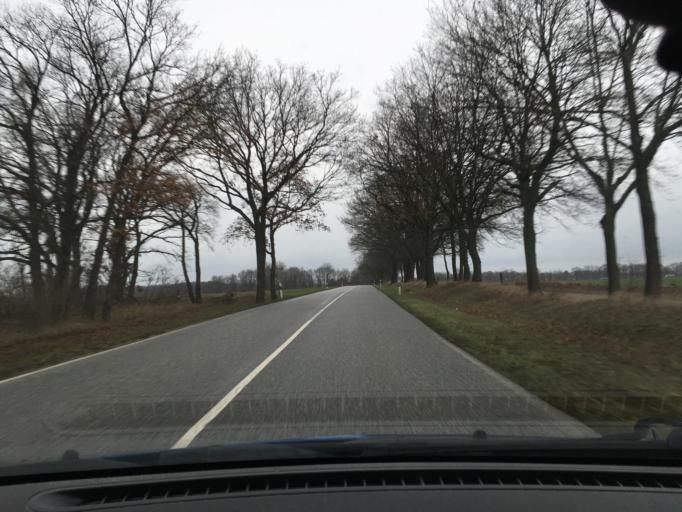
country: DE
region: Schleswig-Holstein
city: Lanze
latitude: 53.3841
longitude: 10.6280
